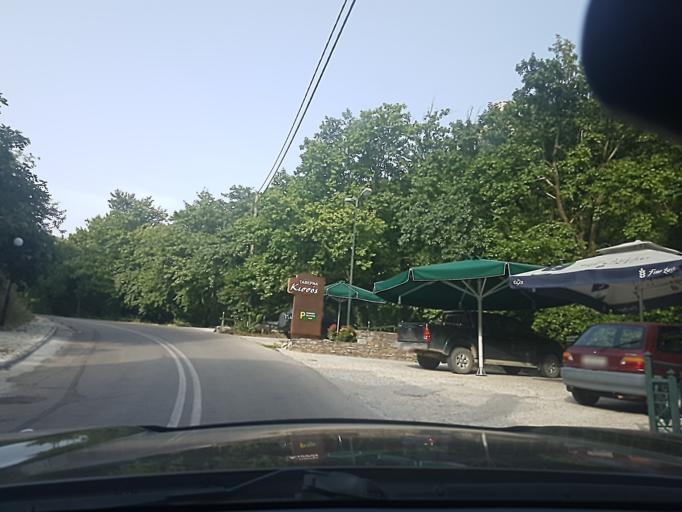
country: GR
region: Central Greece
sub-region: Nomos Evvoias
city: Yimnon
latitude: 38.5827
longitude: 23.8396
